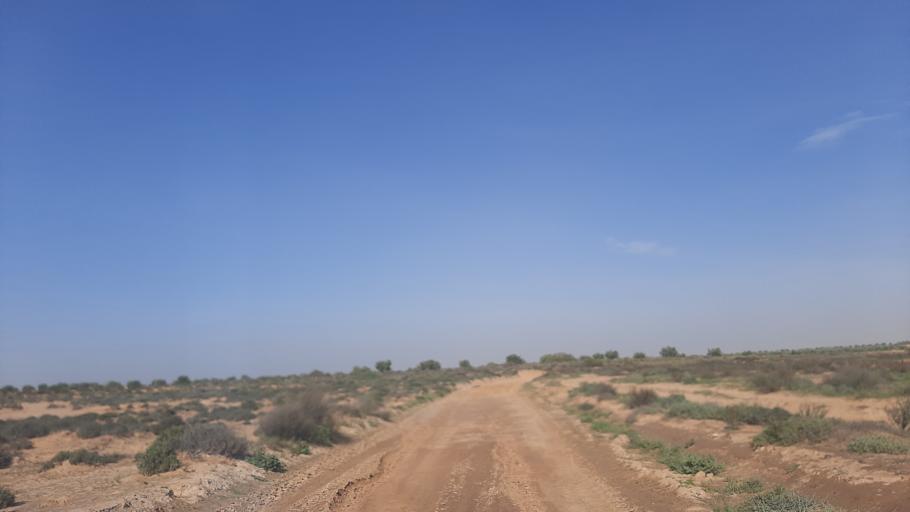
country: TN
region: Madanin
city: Zarzis
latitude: 33.4510
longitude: 10.8083
